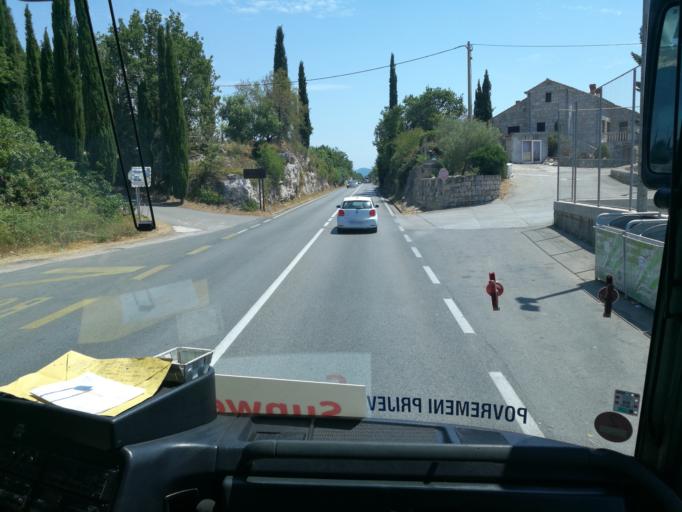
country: HR
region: Dubrovacko-Neretvanska
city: Jasenice
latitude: 42.5628
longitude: 18.2522
